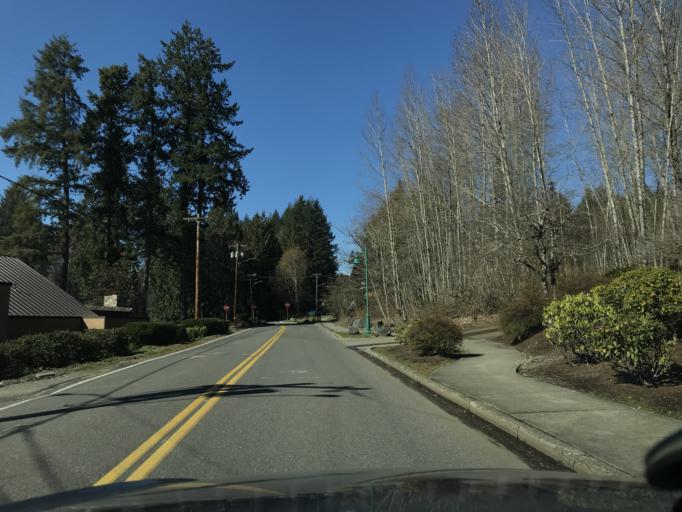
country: US
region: Washington
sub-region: Pierce County
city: Gig Harbor
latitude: 47.3413
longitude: -122.5957
